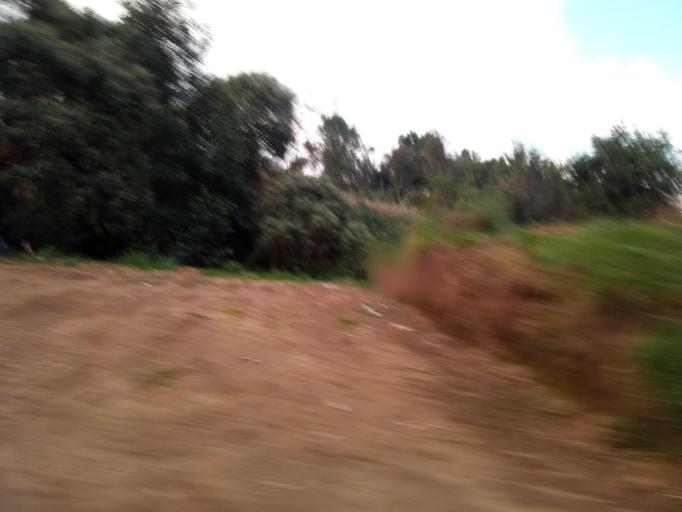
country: GT
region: Quetzaltenango
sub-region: Municipio de La Esperanza
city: La Esperanza
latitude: 14.8487
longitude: -91.5538
